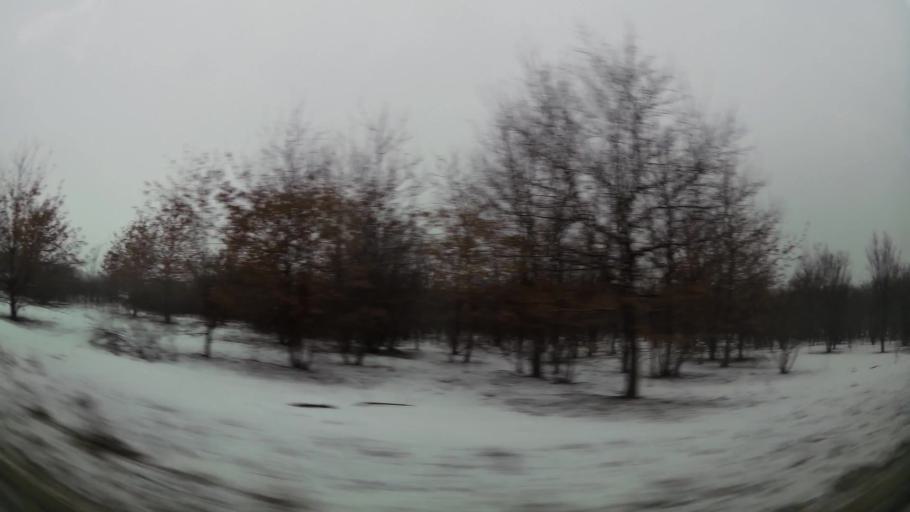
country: RS
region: Central Serbia
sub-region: Belgrade
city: Cukarica
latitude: 44.7552
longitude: 20.3821
